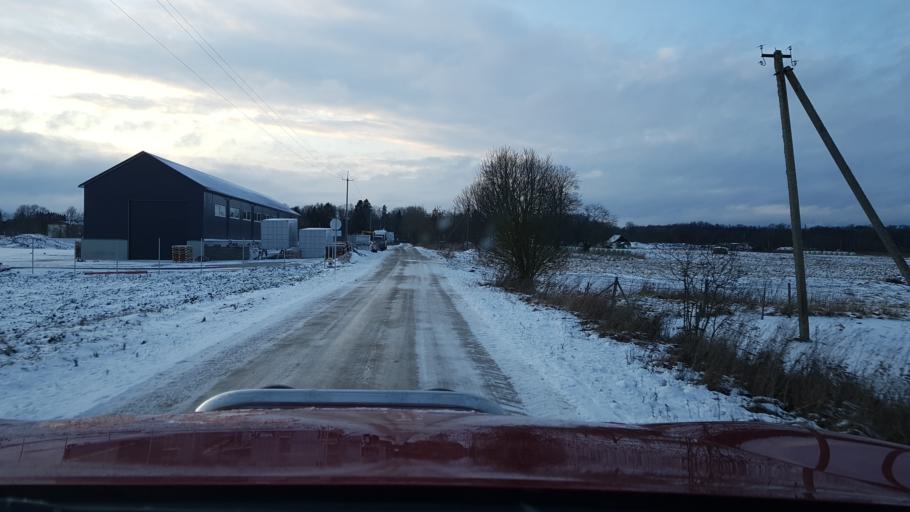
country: EE
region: Harju
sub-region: Maardu linn
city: Maardu
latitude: 59.4293
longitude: 25.0287
